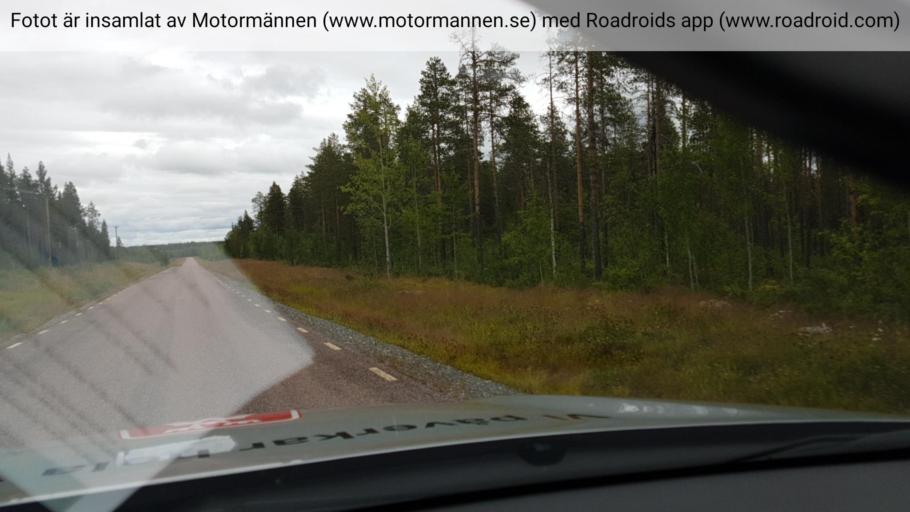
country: SE
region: Norrbotten
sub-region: Pajala Kommun
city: Pajala
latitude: 66.9387
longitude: 22.9872
